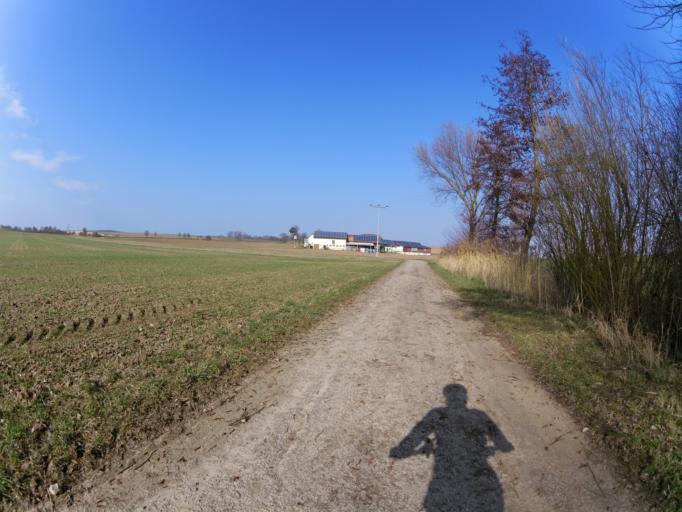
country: DE
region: Bavaria
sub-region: Regierungsbezirk Unterfranken
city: Sulzdorf
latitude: 49.6521
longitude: 9.9182
